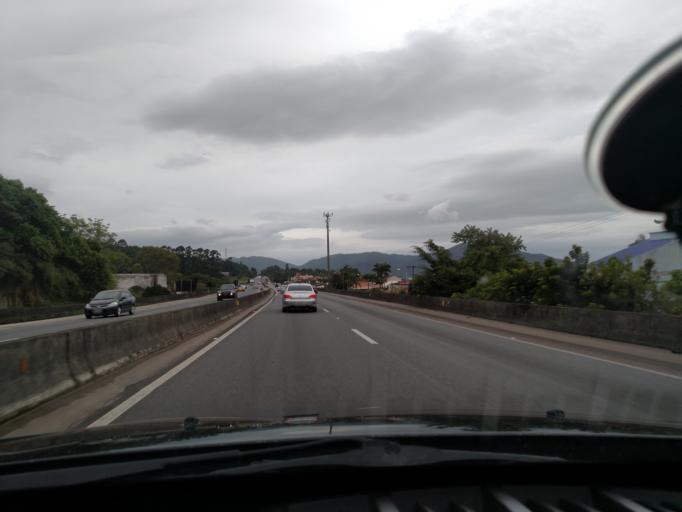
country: BR
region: Santa Catarina
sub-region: Biguacu
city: Biguacu
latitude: -27.4536
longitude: -48.6352
